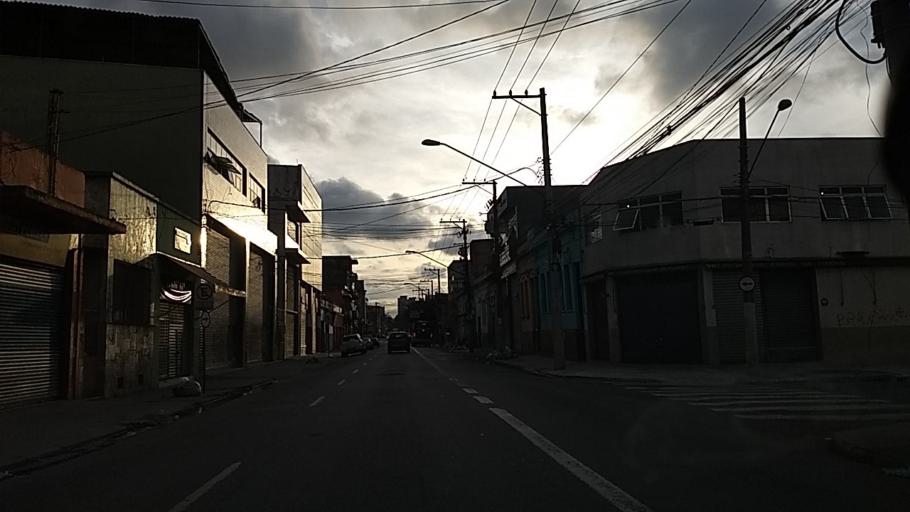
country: BR
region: Sao Paulo
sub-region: Sao Paulo
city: Sao Paulo
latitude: -23.5348
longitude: -46.6233
